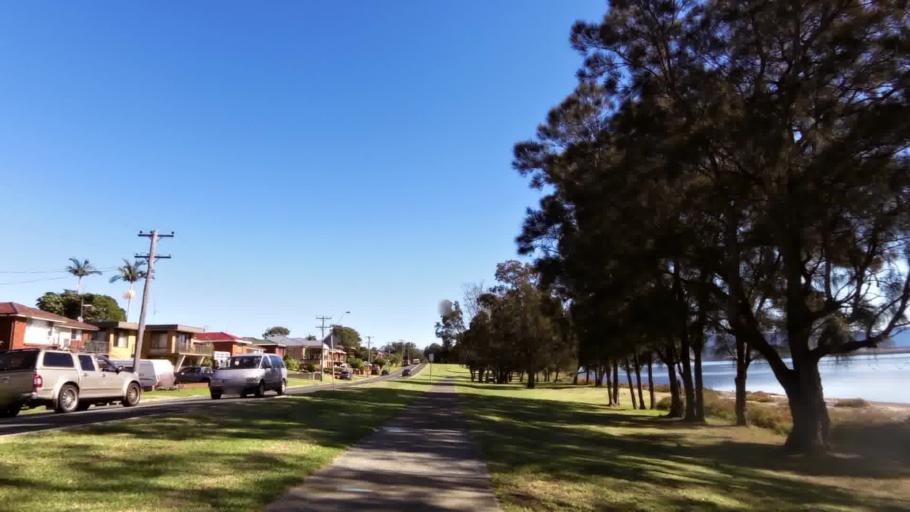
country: AU
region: New South Wales
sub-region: Shellharbour
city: Lake Illawarra
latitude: -34.5423
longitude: 150.8463
